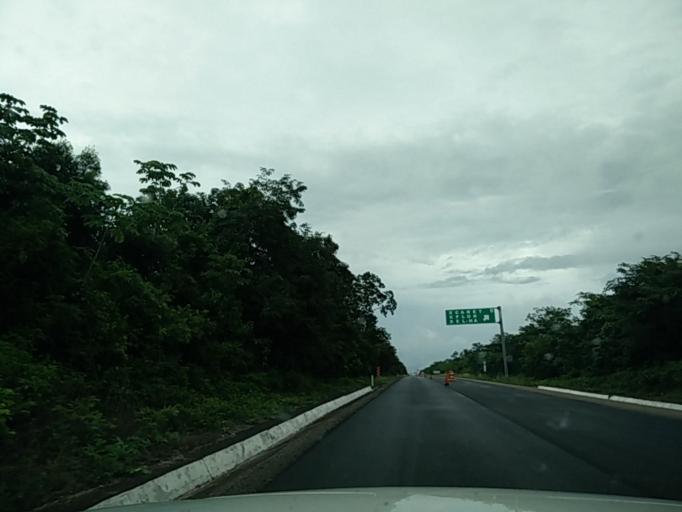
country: MX
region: Quintana Roo
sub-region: Lazaro Cardenas
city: El Tintal
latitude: 20.9009
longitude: -87.4638
